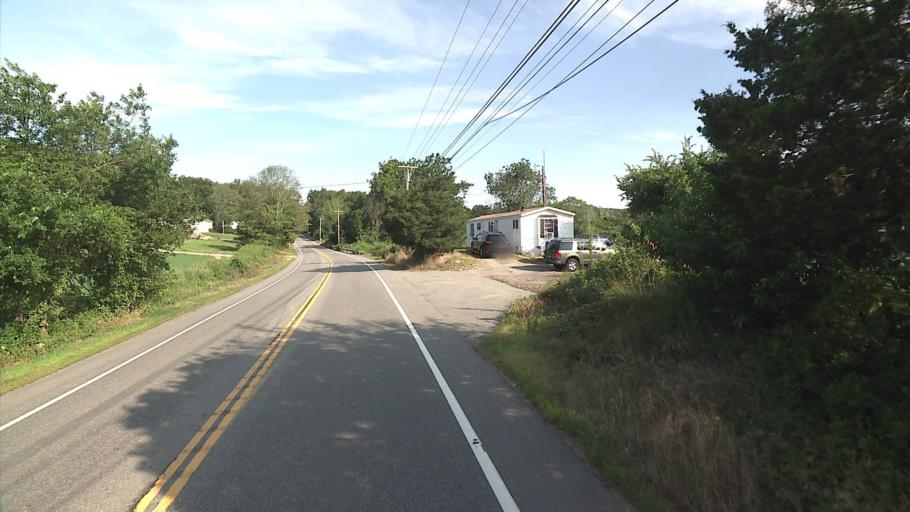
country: US
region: Connecticut
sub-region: New London County
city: Pawcatuck
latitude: 41.4346
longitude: -71.8693
